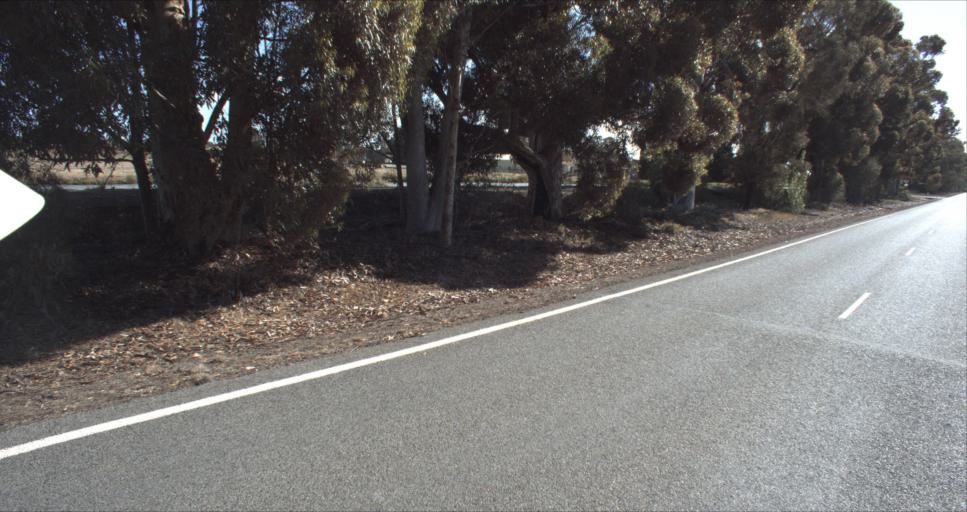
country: AU
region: New South Wales
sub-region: Leeton
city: Leeton
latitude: -34.5459
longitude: 146.3270
